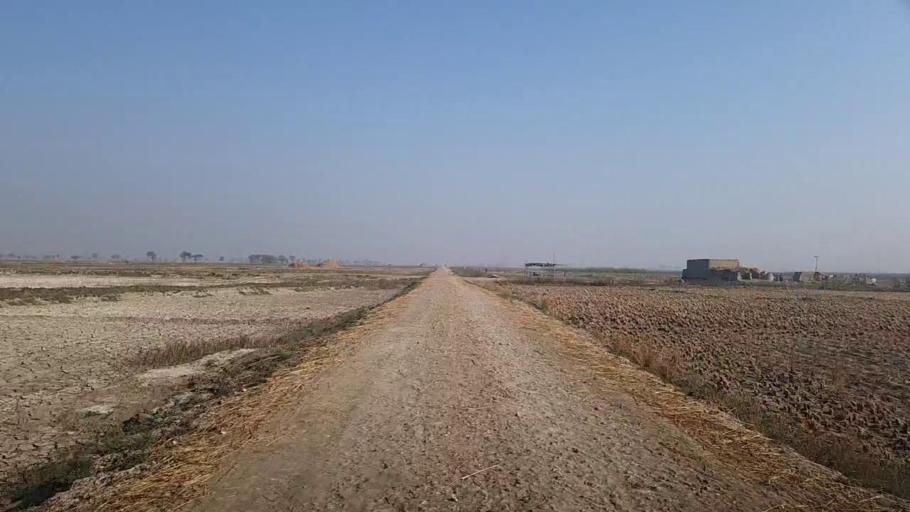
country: PK
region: Sindh
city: Radhan
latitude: 27.1342
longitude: 67.9044
